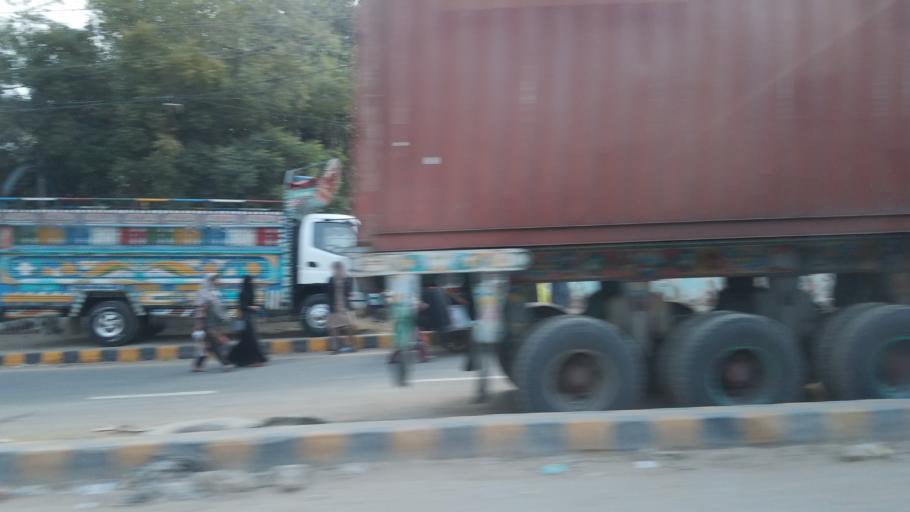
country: PK
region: Sindh
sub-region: Karachi District
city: Karachi
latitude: 24.9388
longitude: 67.0852
